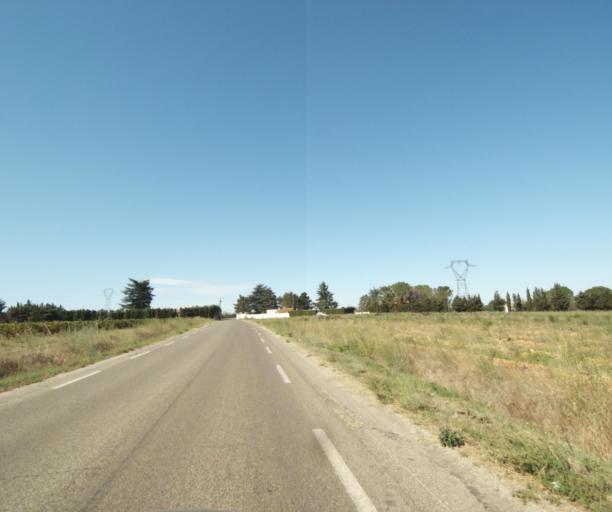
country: FR
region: Languedoc-Roussillon
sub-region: Departement du Gard
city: Bouillargues
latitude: 43.8094
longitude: 4.4429
